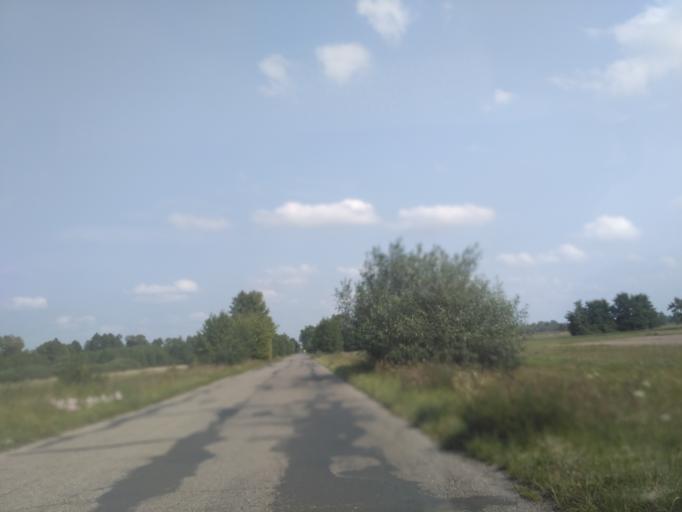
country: PL
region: Lublin Voivodeship
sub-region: Powiat wlodawski
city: Urszulin
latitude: 51.3815
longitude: 23.1776
